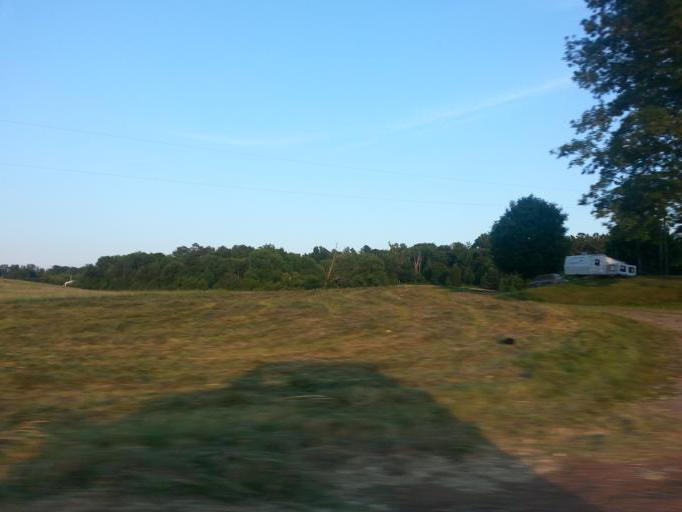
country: US
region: Tennessee
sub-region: Monroe County
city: Sweetwater
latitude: 35.6432
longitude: -84.4294
